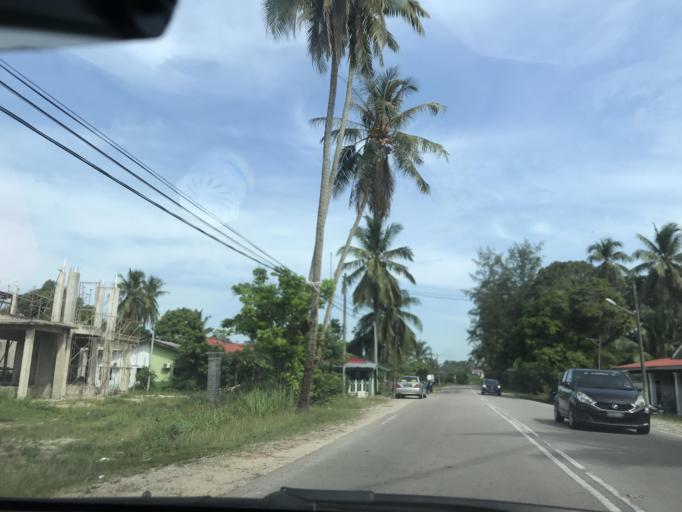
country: MY
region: Kelantan
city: Tumpat
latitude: 6.2149
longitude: 102.1266
